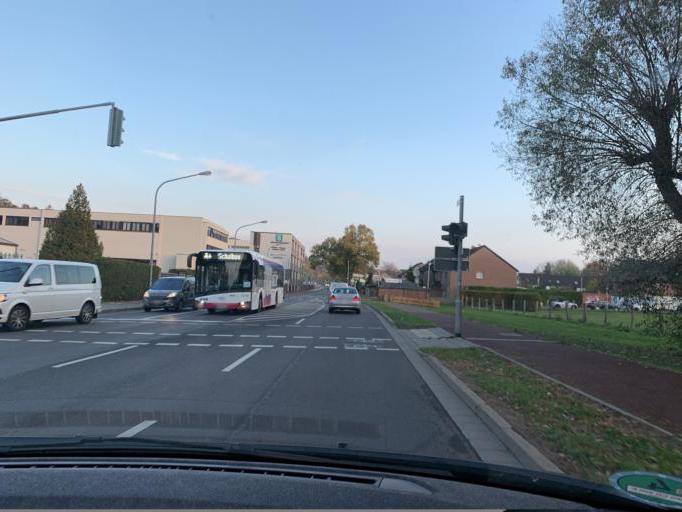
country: DE
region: North Rhine-Westphalia
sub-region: Regierungsbezirk Dusseldorf
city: Monchengladbach
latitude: 51.1469
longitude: 6.4502
